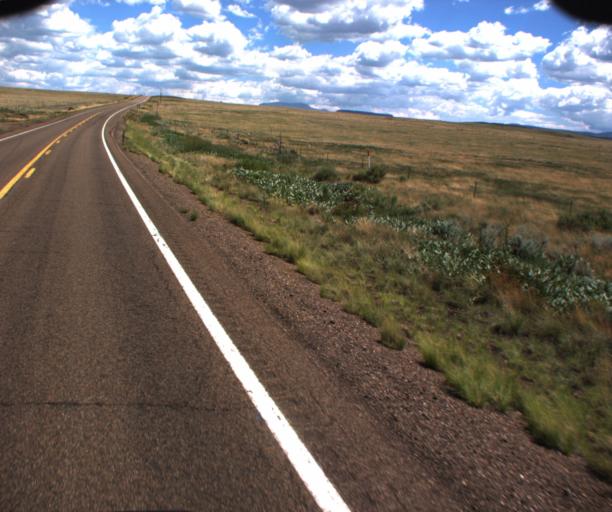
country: US
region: Arizona
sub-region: Apache County
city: Springerville
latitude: 34.1865
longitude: -109.3351
